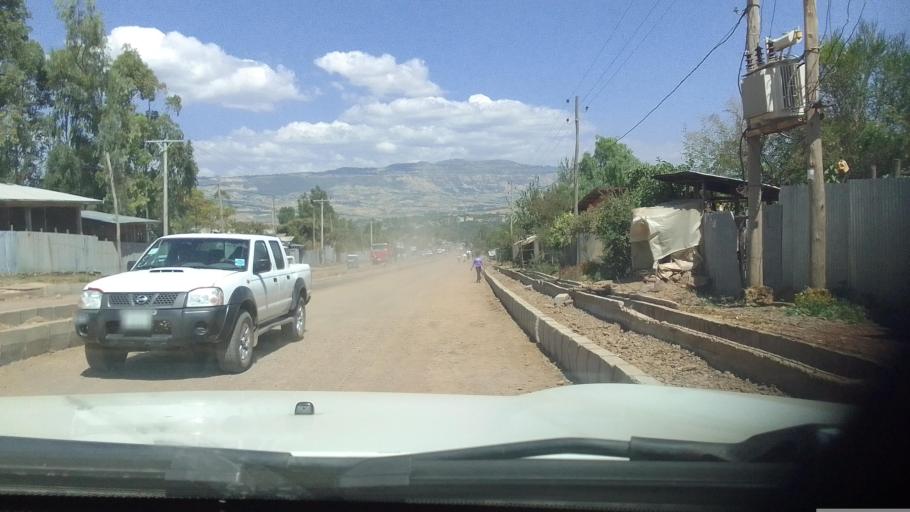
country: ET
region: Oromiya
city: Hagere Hiywet
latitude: 8.9675
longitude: 37.8475
